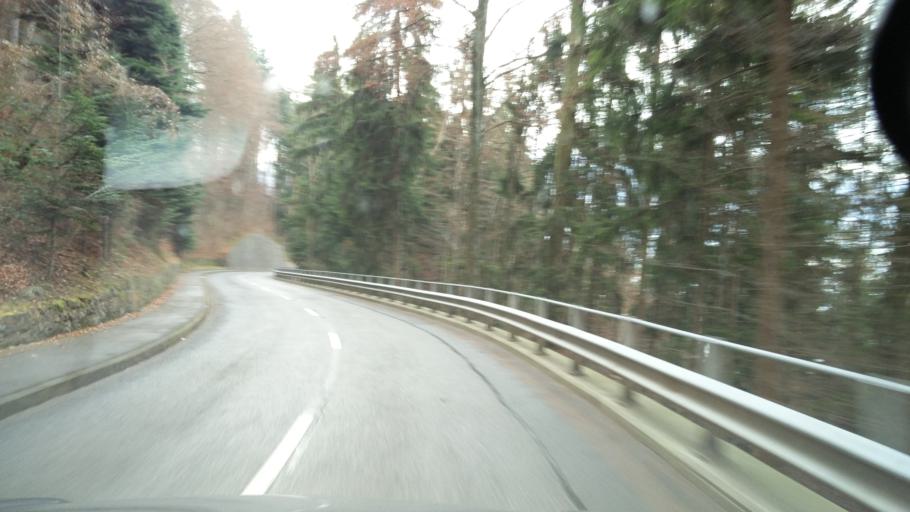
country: LI
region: Planken
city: Planken
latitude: 47.1818
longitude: 9.5408
